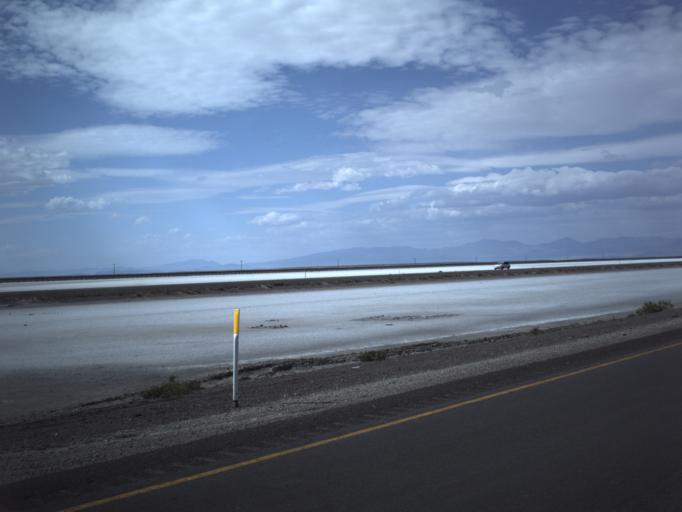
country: US
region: Utah
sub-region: Tooele County
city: Wendover
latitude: 40.7361
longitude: -113.6897
